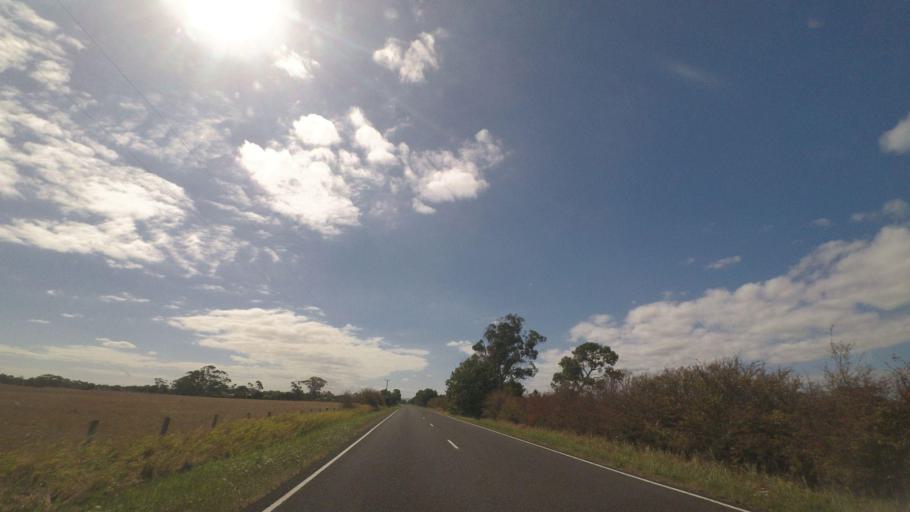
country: AU
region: Victoria
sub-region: Cardinia
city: Garfield
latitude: -38.1994
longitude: 145.6283
